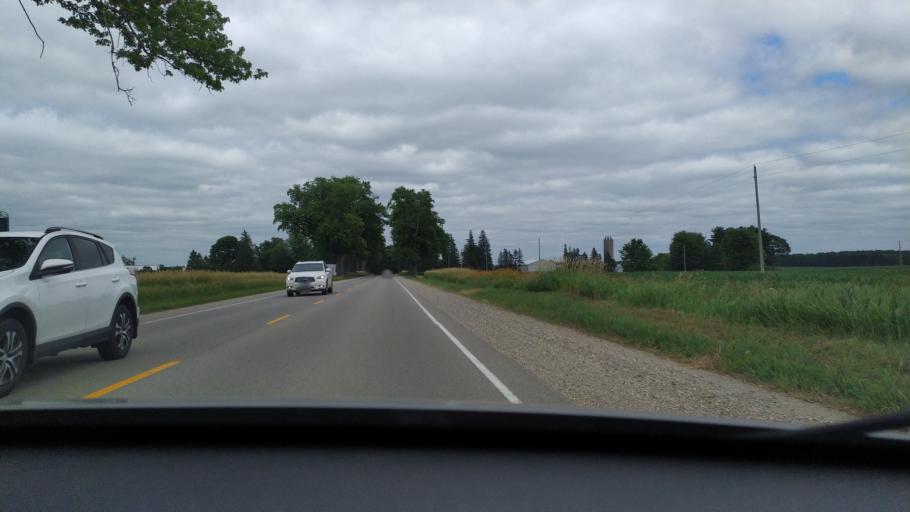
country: CA
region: Ontario
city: Stratford
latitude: 43.3160
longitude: -80.9684
